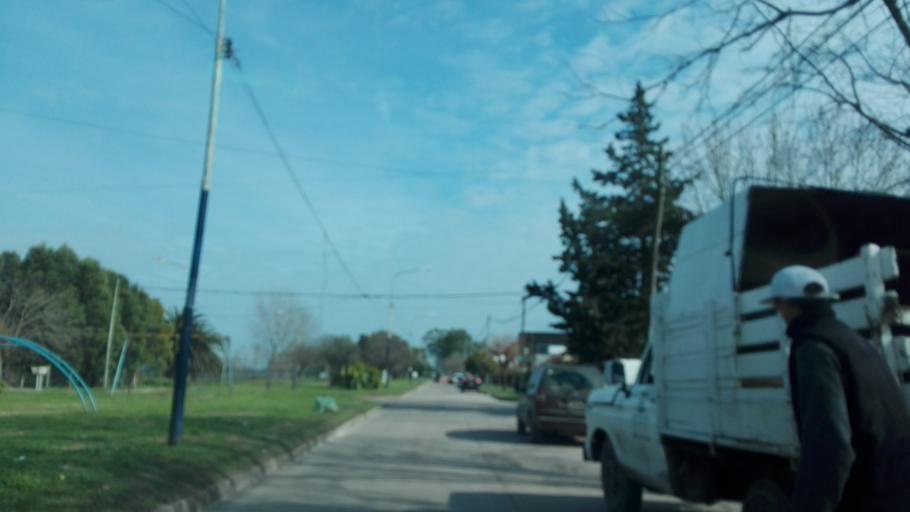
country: AR
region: Buenos Aires
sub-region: Partido de Chascomus
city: Chascomus
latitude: -35.5686
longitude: -58.0210
